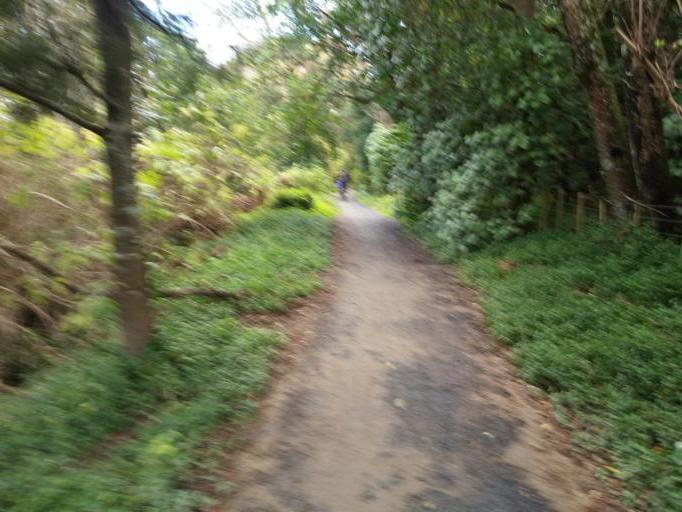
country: NZ
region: Wellington
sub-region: Kapiti Coast District
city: Paraparaumu
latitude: -40.8758
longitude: 175.0374
